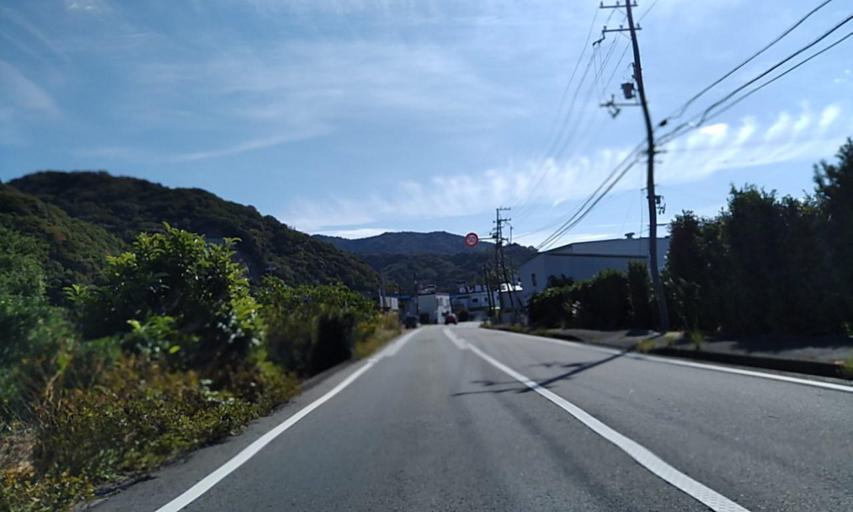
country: JP
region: Wakayama
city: Kainan
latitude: 34.0158
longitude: 135.1863
